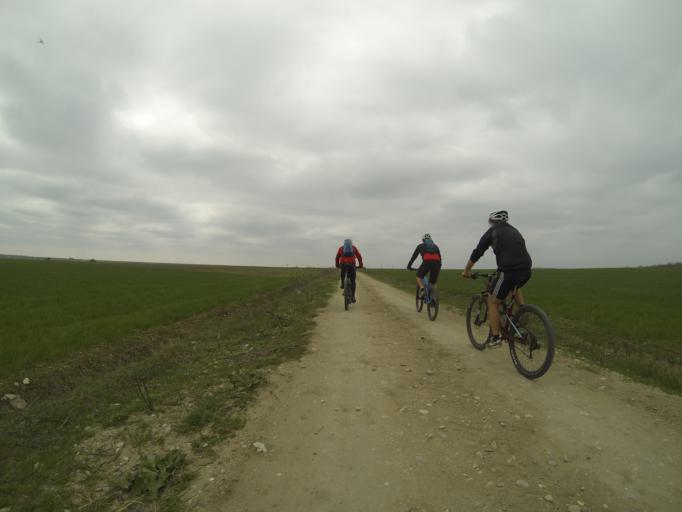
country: RO
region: Dolj
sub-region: Comuna Predesti
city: Predesti
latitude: 44.3373
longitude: 23.6254
